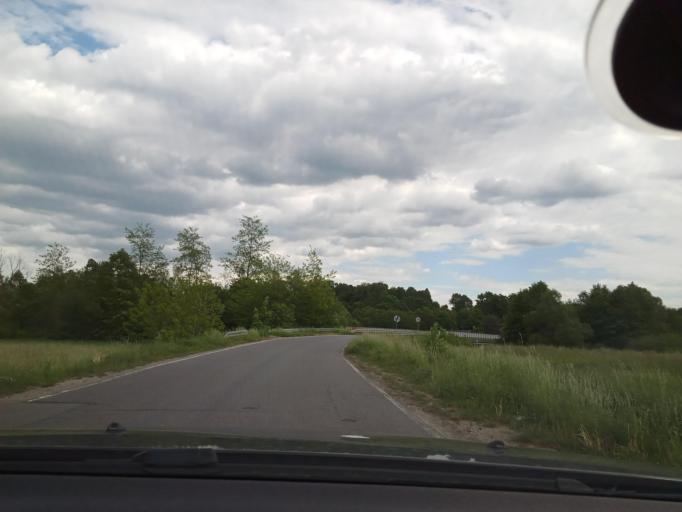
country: PL
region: Lesser Poland Voivodeship
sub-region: Powiat bochenski
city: Lapanow
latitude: 49.8316
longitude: 20.2995
